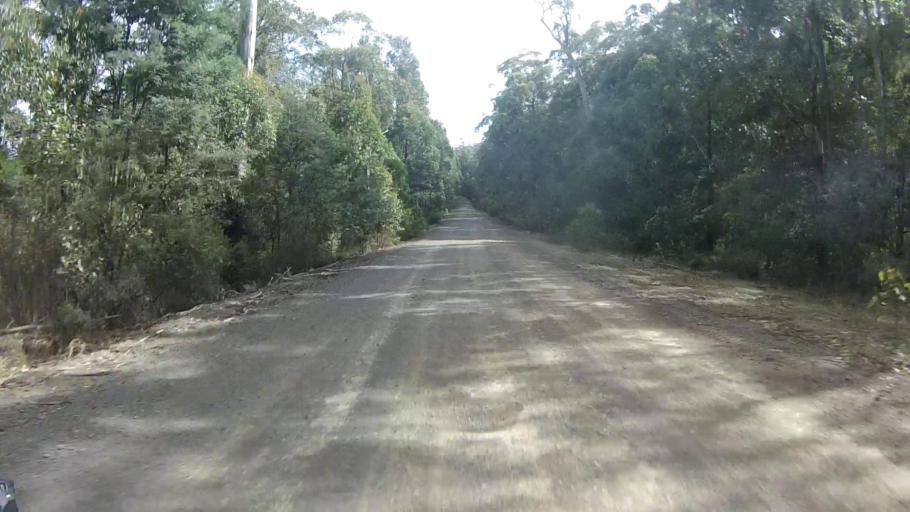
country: AU
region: Tasmania
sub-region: Sorell
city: Sorell
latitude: -42.7502
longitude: 147.8285
